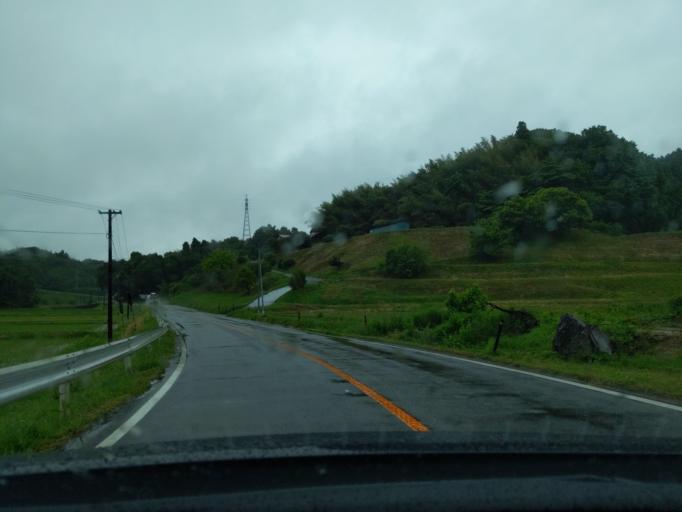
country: JP
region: Fukushima
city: Nihommatsu
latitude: 37.5448
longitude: 140.4974
